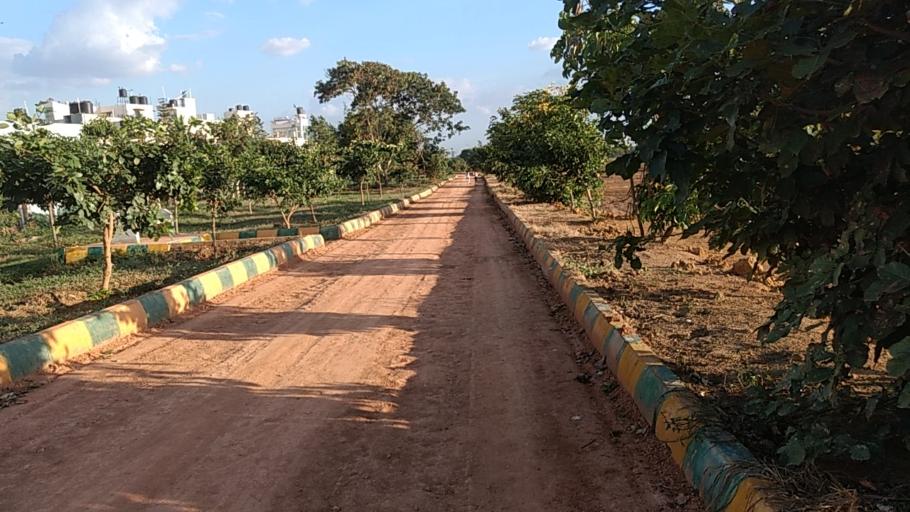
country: IN
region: Karnataka
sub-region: Bangalore Urban
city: Yelahanka
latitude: 13.0679
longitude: 77.5639
